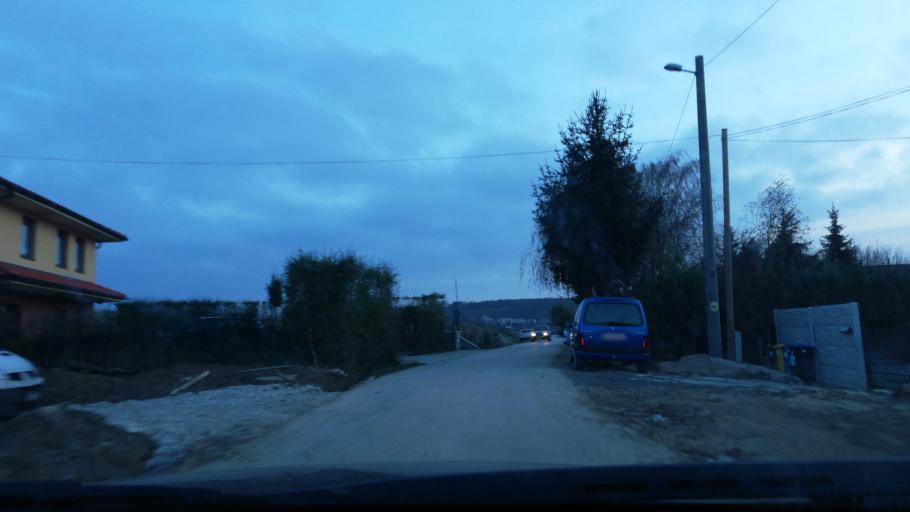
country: SK
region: Nitriansky
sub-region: Okres Nitra
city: Nitra
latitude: 48.3159
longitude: 17.9952
